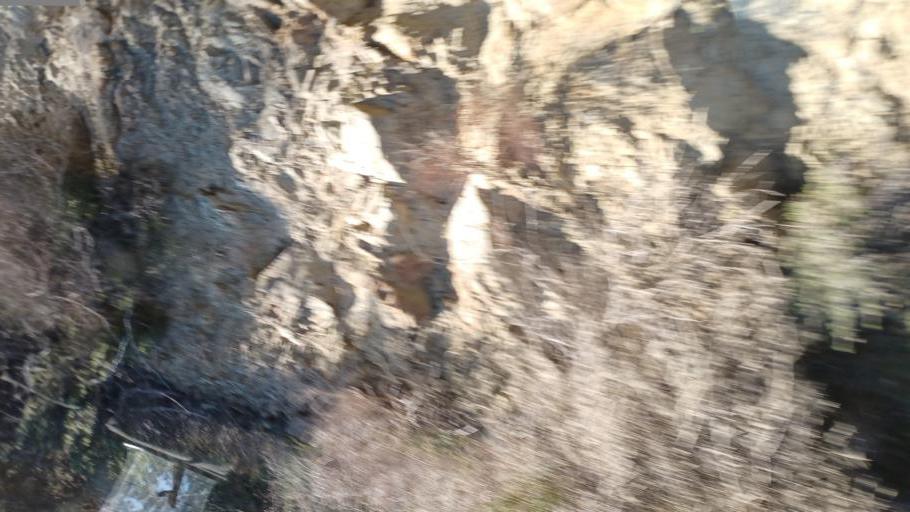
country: CY
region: Pafos
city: Polis
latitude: 35.0139
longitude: 32.4947
